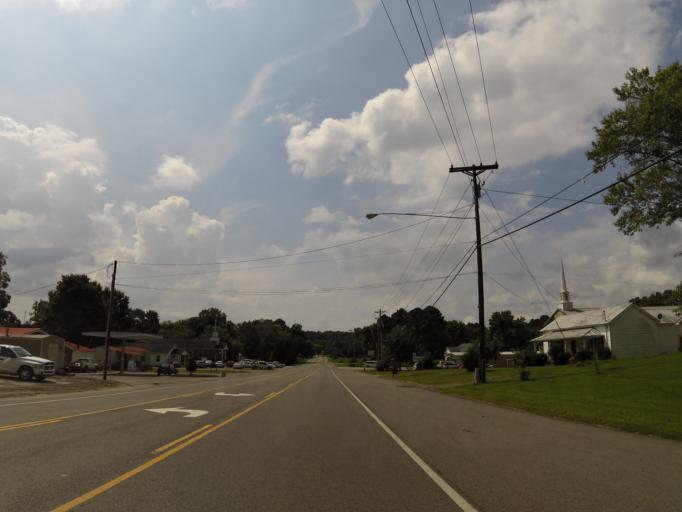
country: US
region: Tennessee
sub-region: Perry County
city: Linden
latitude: 35.7687
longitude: -87.7841
